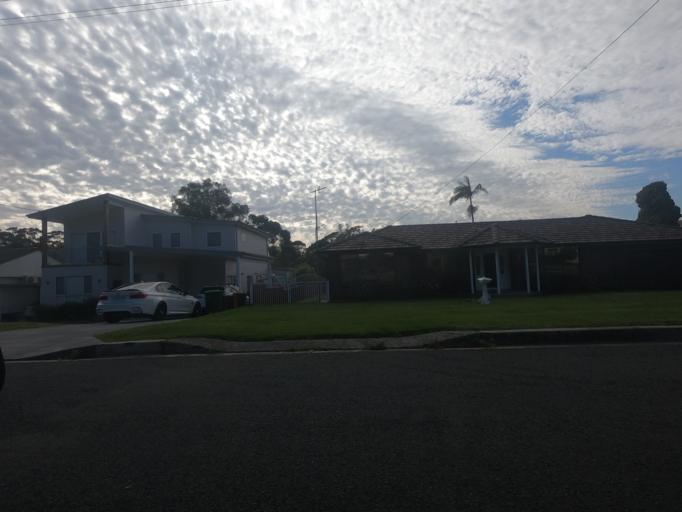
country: AU
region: New South Wales
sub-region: Wollongong
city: Corrimal
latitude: -34.3571
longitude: 150.8962
